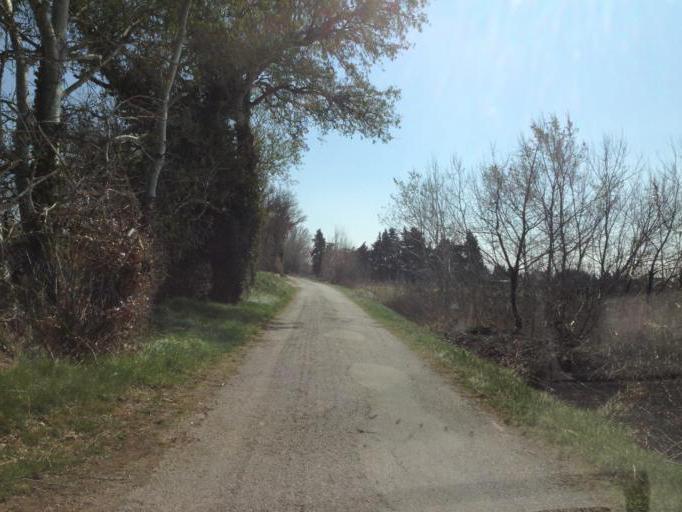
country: FR
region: Provence-Alpes-Cote d'Azur
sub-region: Departement du Vaucluse
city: Courthezon
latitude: 44.0812
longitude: 4.9231
